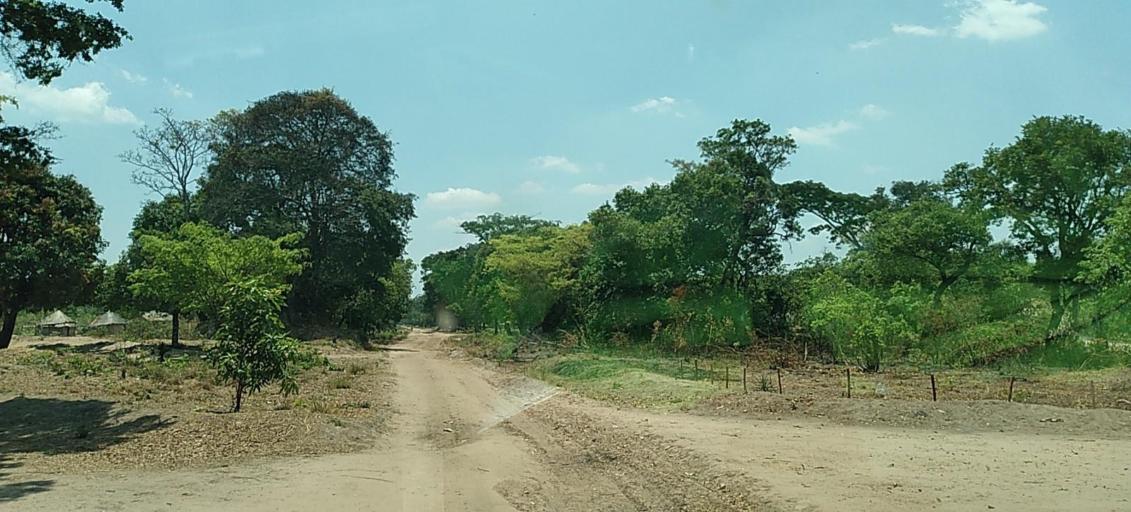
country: CD
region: Katanga
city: Kolwezi
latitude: -11.3725
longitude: 25.2142
